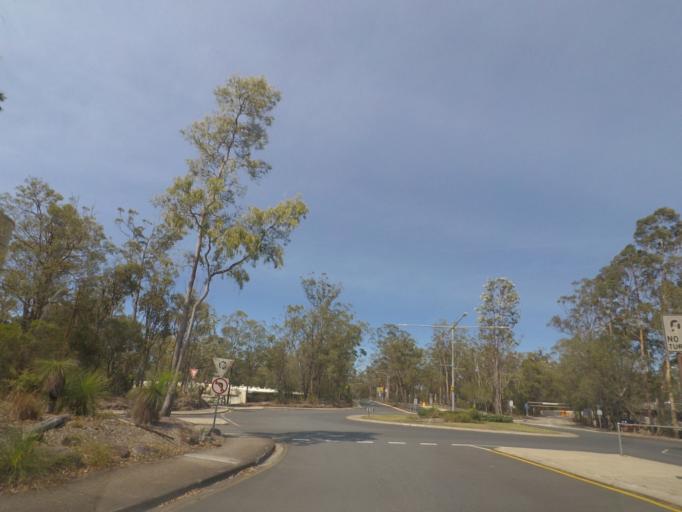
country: AU
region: Queensland
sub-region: Brisbane
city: Nathan
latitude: -27.5542
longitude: 153.0552
